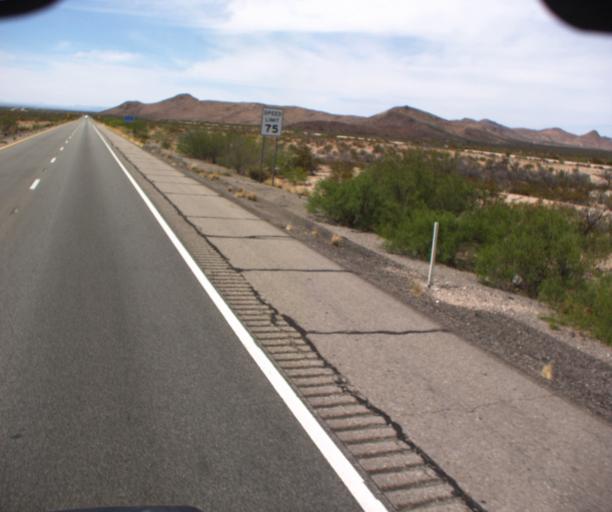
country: US
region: New Mexico
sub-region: Hidalgo County
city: Lordsburg
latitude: 32.2325
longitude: -109.0653
